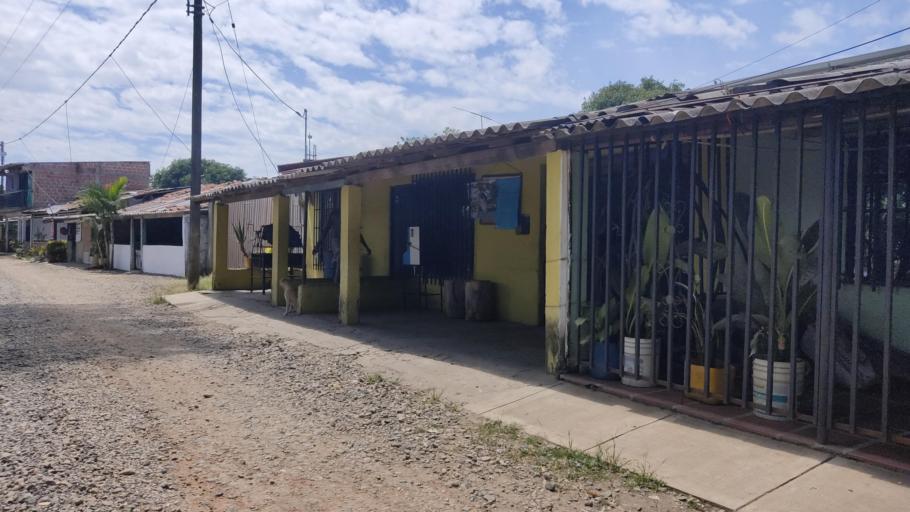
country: CO
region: Valle del Cauca
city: Jamundi
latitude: 3.1615
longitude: -76.5119
